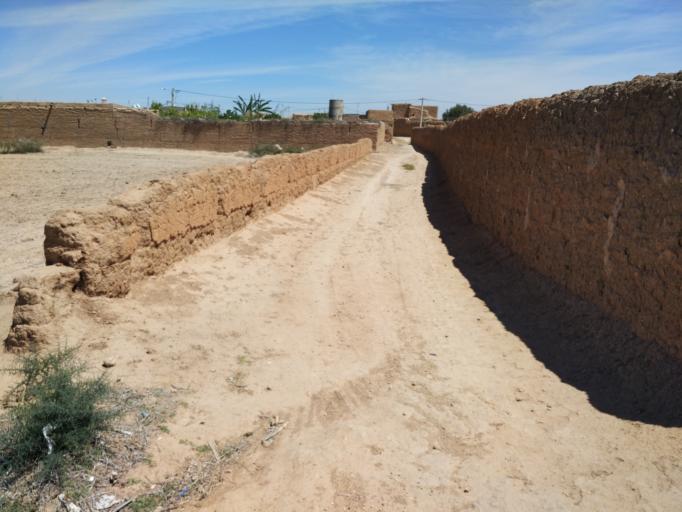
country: MA
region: Marrakech-Tensift-Al Haouz
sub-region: Marrakech
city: Marrakesh
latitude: 31.6404
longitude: -8.2963
